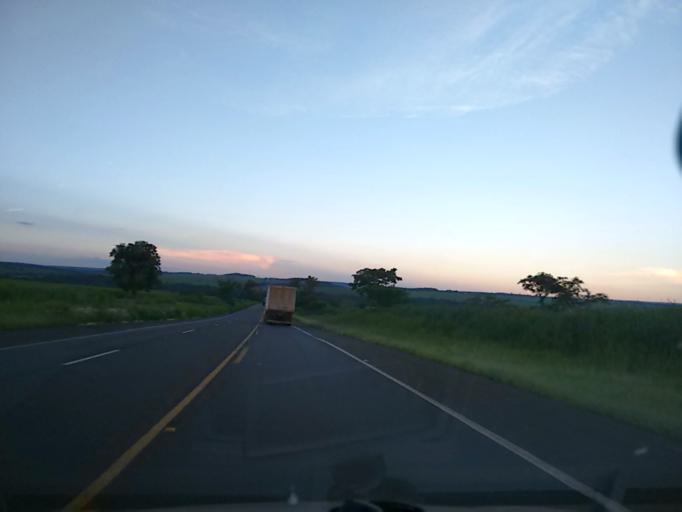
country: BR
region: Sao Paulo
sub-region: Boa Esperanca Do Sul
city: Boa Esperanca do Sul
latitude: -22.0915
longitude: -48.4491
